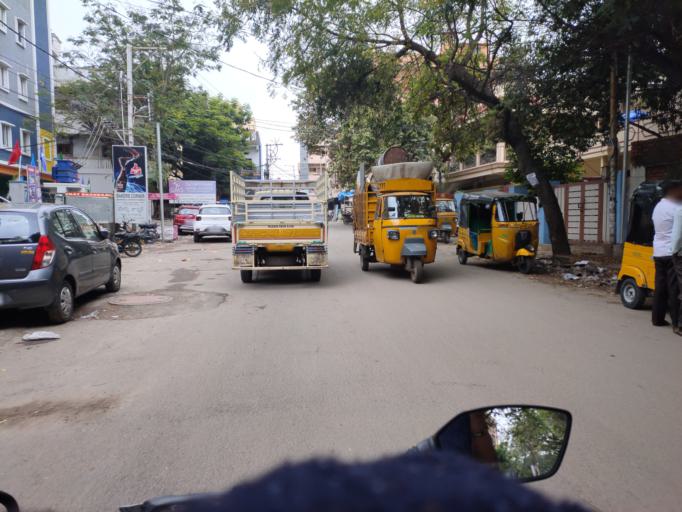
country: IN
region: Telangana
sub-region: Rangareddi
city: Kukatpalli
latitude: 17.4491
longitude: 78.4474
